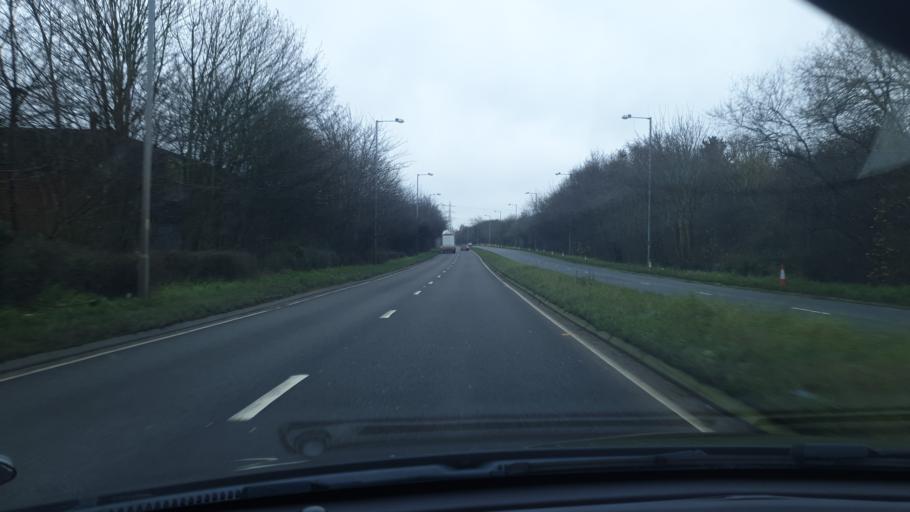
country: GB
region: England
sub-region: Walsall
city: Willenhall
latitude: 52.5815
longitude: -2.0653
